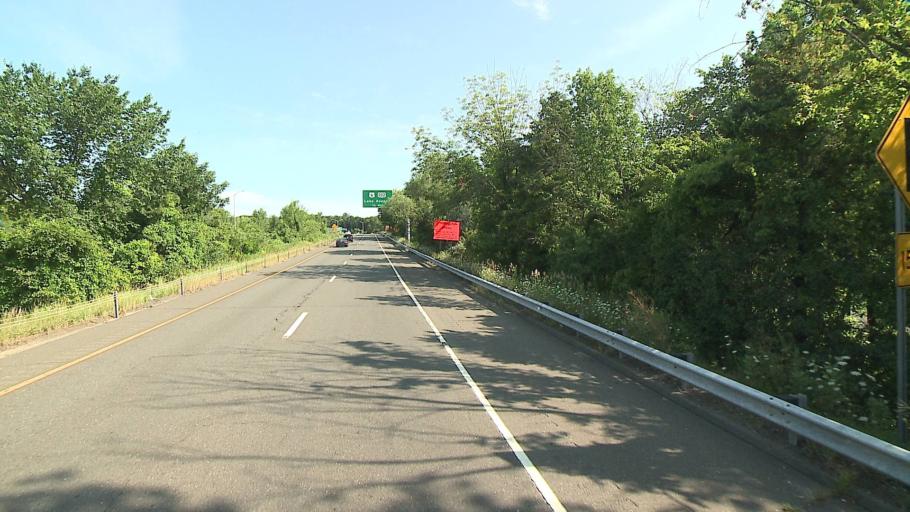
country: US
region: Connecticut
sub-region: Fairfield County
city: Danbury
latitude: 41.3856
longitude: -73.4757
